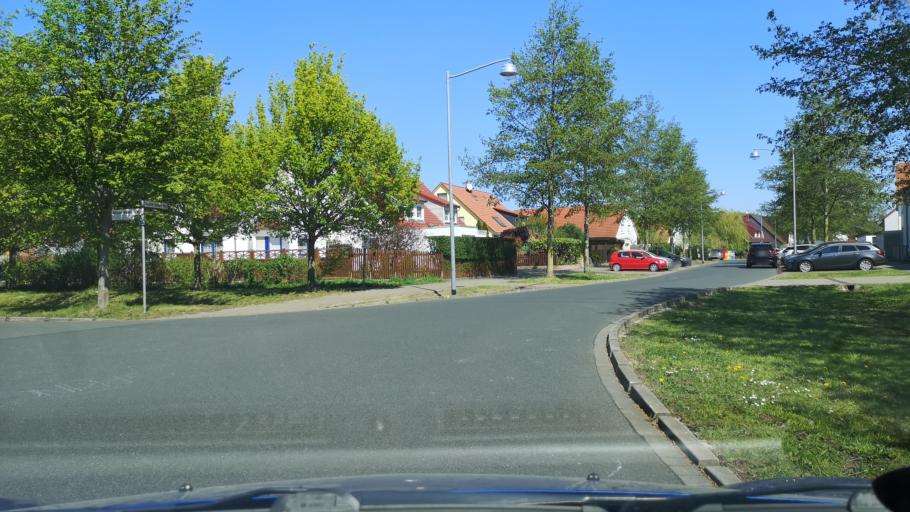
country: DE
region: Lower Saxony
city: Langenhagen
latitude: 52.4797
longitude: 9.7303
